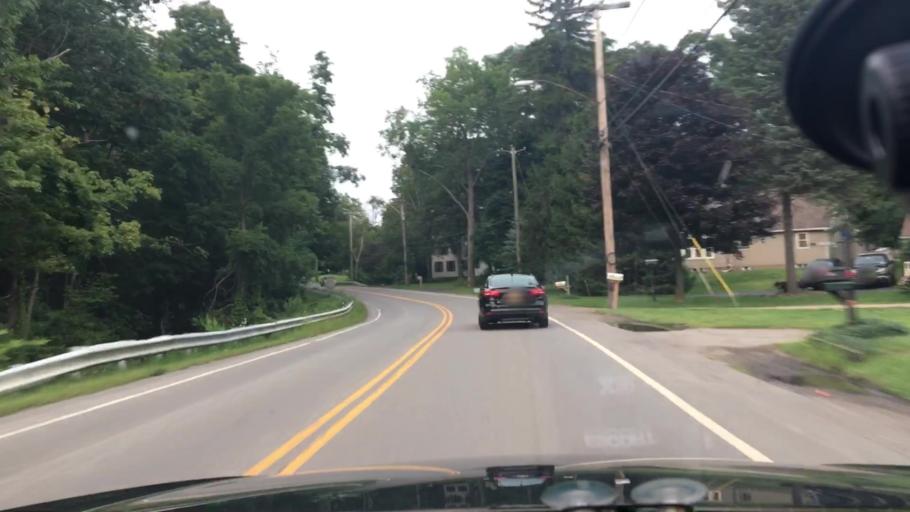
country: US
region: New York
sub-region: Erie County
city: Hamburg
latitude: 42.7329
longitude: -78.8076
